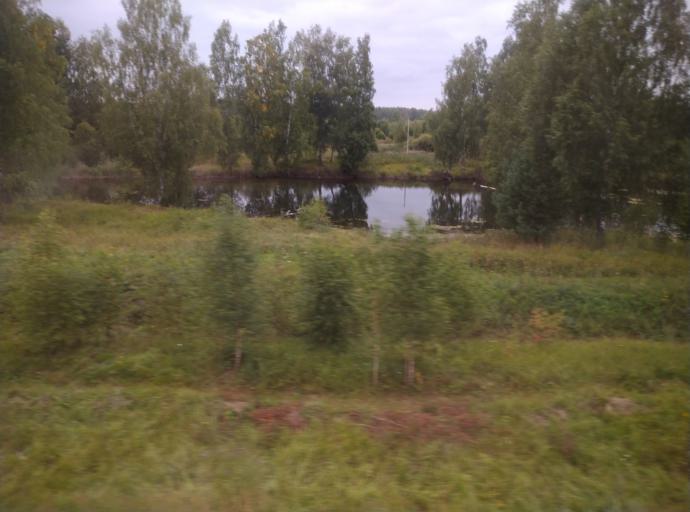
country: RU
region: Kostroma
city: Kosmynino
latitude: 57.5938
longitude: 40.7708
